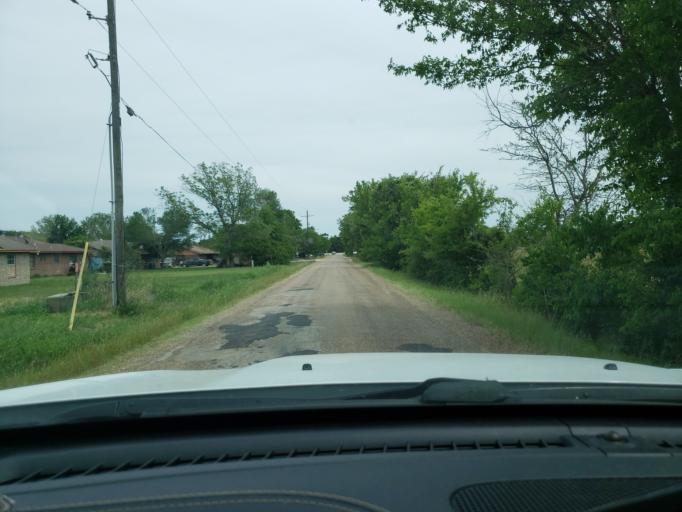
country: US
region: Texas
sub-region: Burleson County
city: Somerville
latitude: 30.3507
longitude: -96.5427
